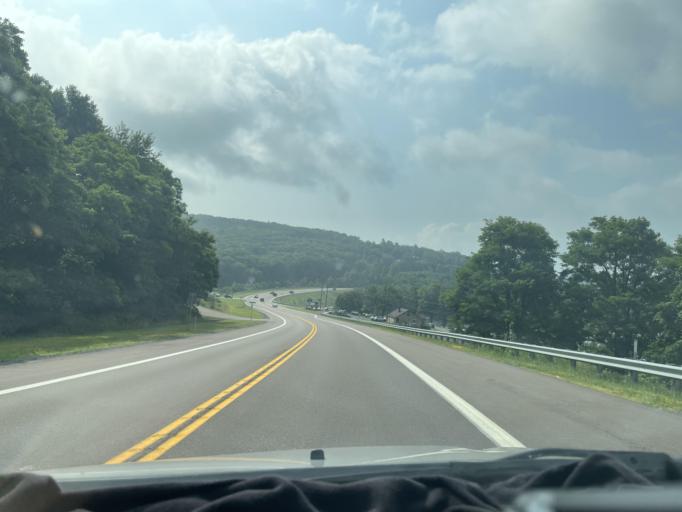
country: US
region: Maryland
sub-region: Garrett County
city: Oakland
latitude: 39.5396
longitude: -79.3482
